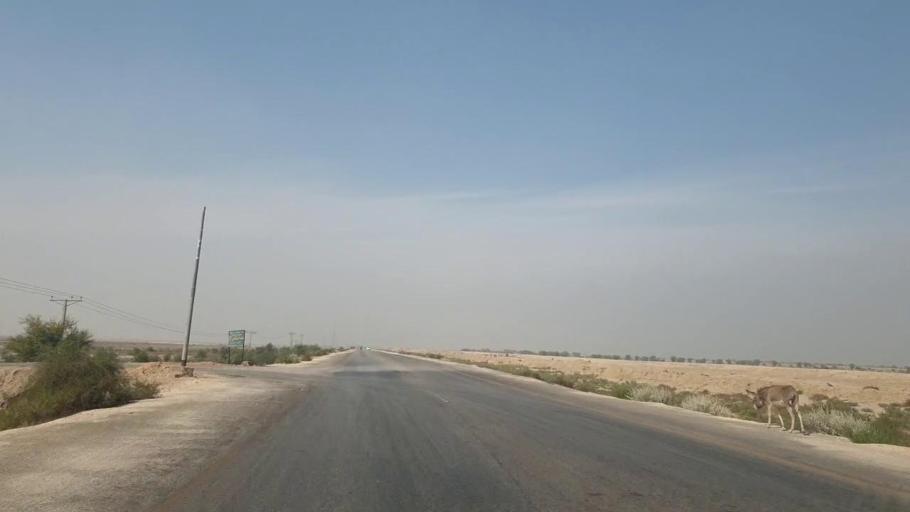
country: PK
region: Sindh
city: Sann
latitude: 25.9108
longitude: 68.2250
